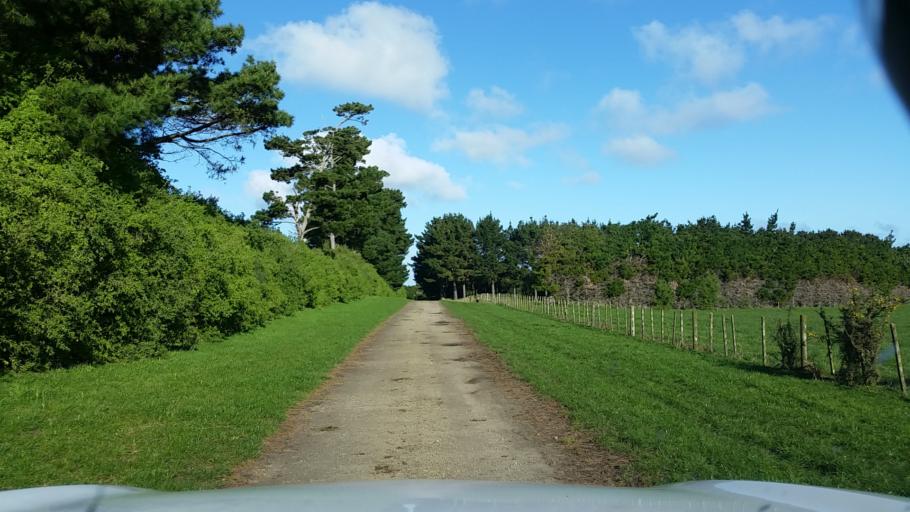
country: NZ
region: Taranaki
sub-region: South Taranaki District
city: Patea
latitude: -39.7405
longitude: 174.5434
